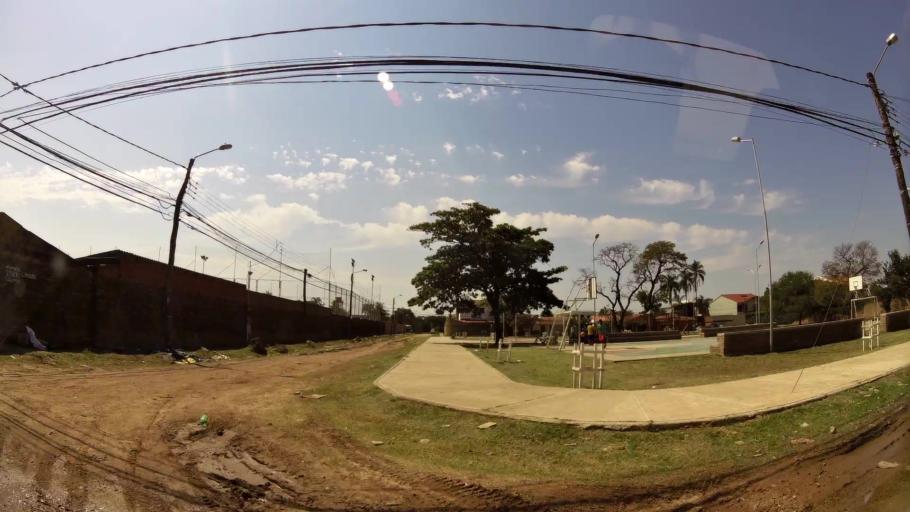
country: BO
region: Santa Cruz
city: Santa Cruz de la Sierra
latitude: -17.7326
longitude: -63.1504
